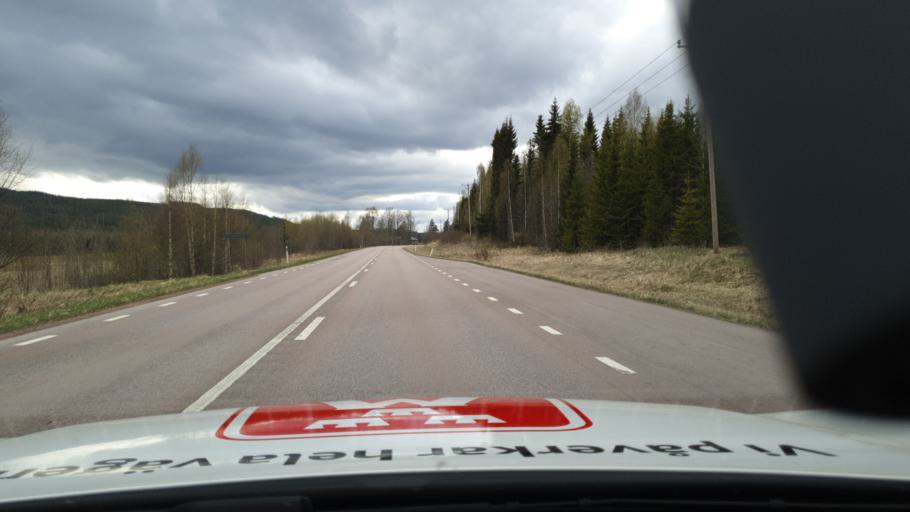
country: SE
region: Jaemtland
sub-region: Braecke Kommun
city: Braecke
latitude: 63.1602
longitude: 15.7342
